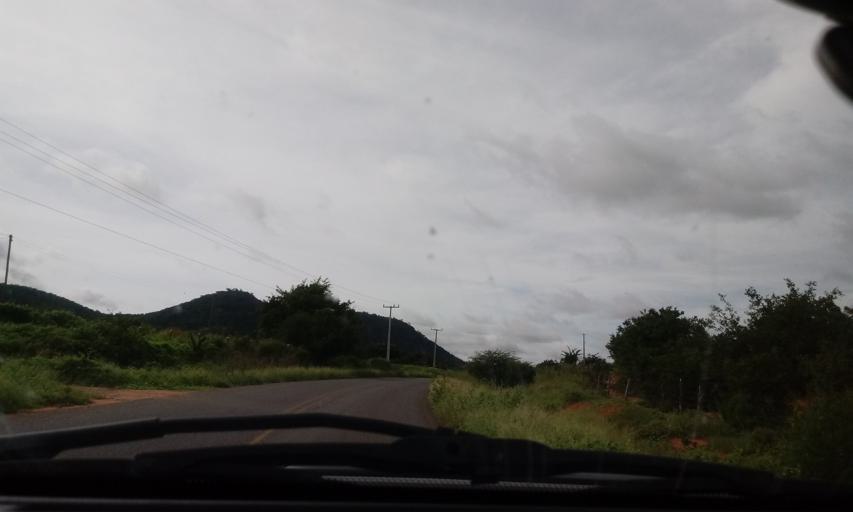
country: BR
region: Bahia
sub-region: Guanambi
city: Guanambi
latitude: -14.1193
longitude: -42.8560
